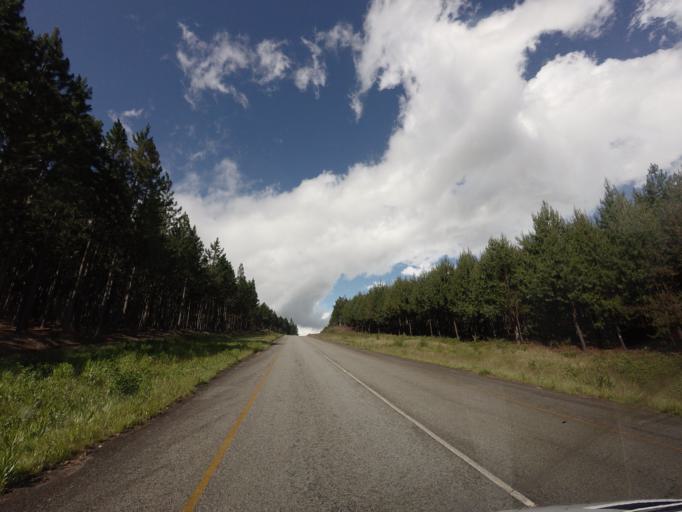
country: ZA
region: Mpumalanga
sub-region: Ehlanzeni District
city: Graksop
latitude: -24.8679
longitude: 30.8477
